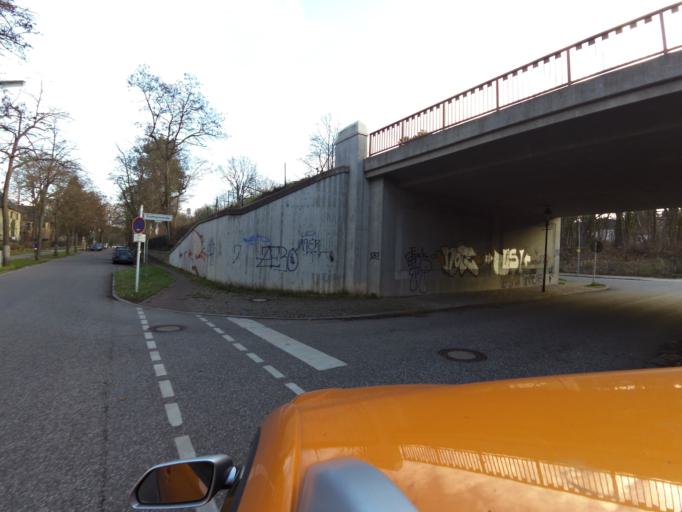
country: DE
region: Berlin
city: Nikolassee
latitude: 52.4375
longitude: 13.2052
